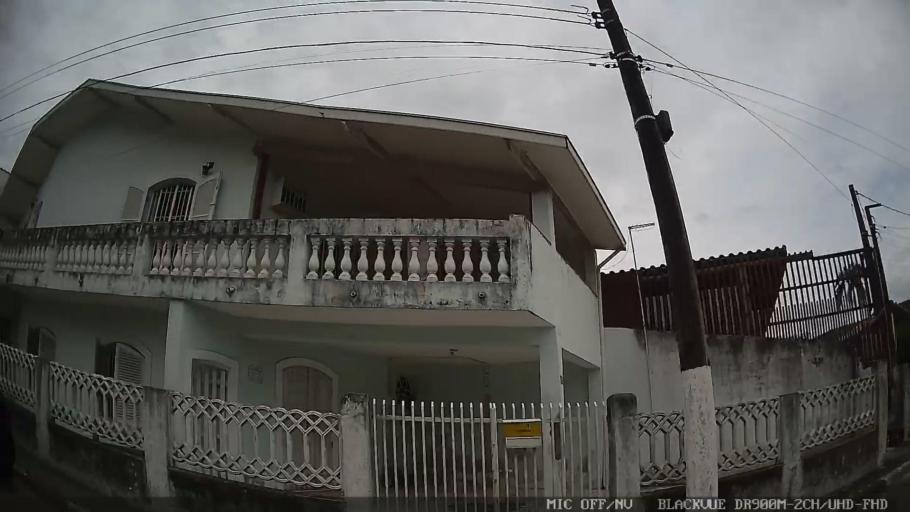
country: BR
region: Sao Paulo
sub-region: Caraguatatuba
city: Caraguatatuba
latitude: -23.6215
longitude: -45.3970
